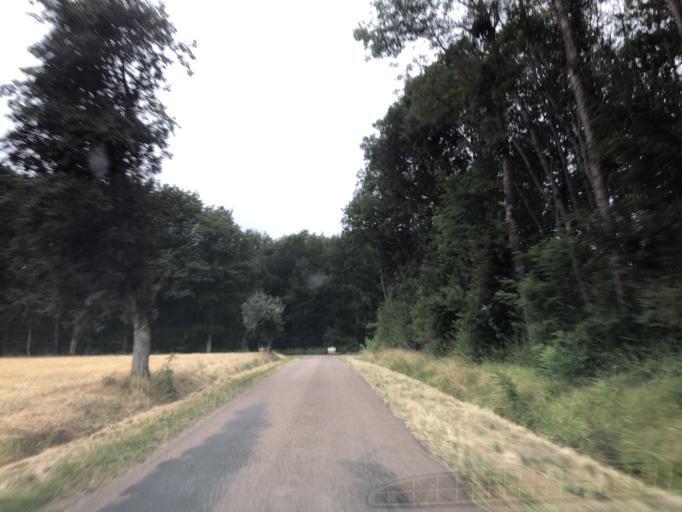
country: FR
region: Bourgogne
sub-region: Departement de l'Yonne
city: Aillant-sur-Tholon
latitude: 47.9002
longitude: 3.3016
